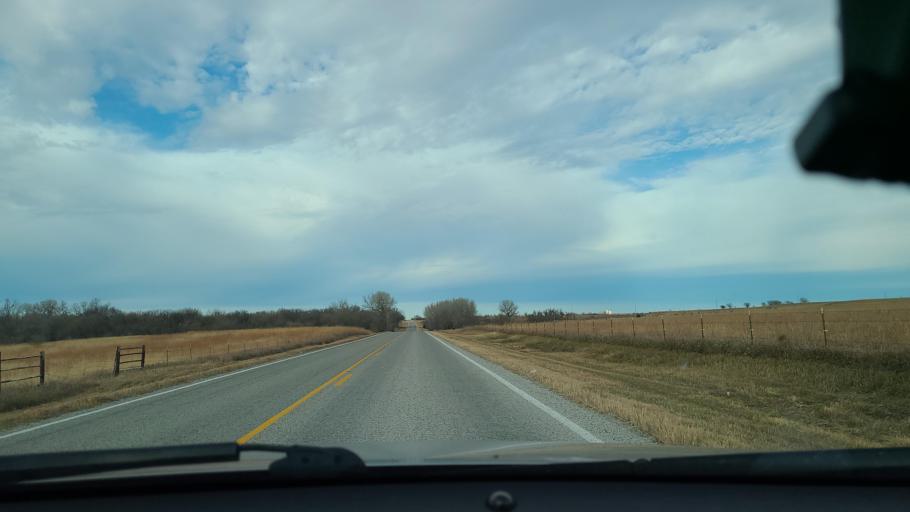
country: US
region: Kansas
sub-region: McPherson County
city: Inman
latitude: 38.3426
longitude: -97.9245
